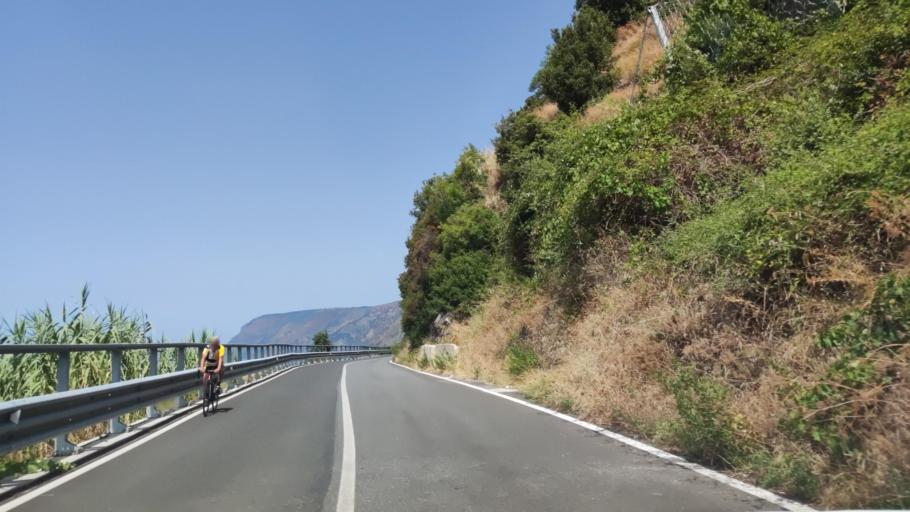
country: IT
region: Calabria
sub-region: Provincia di Reggio Calabria
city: Bagnara Calabra
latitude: 38.2735
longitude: 15.7837
